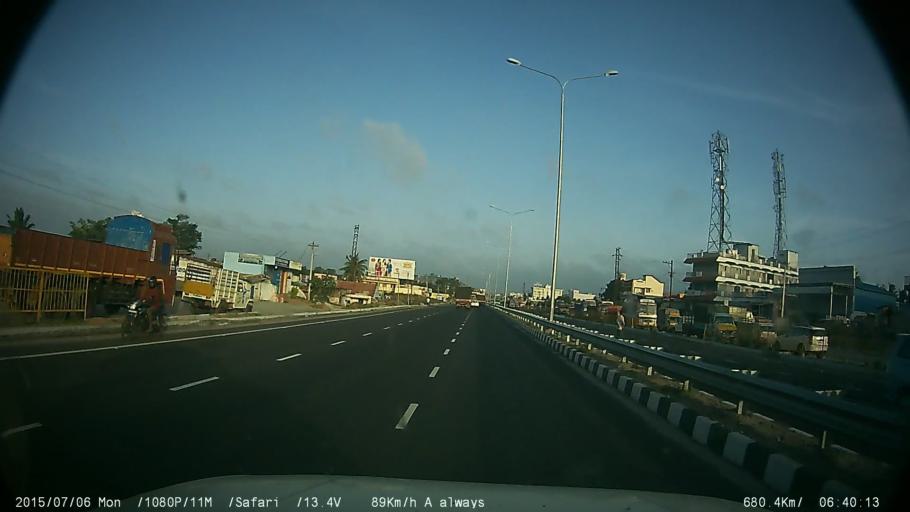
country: IN
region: Tamil Nadu
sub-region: Krishnagiri
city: Hosur
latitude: 12.7251
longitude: 77.8599
